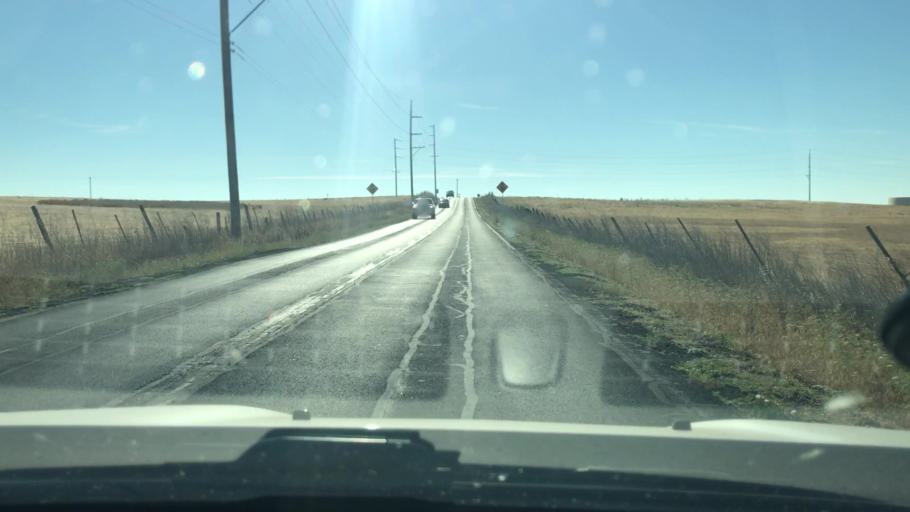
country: US
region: California
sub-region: Solano County
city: Vacaville
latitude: 38.3013
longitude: -121.9371
